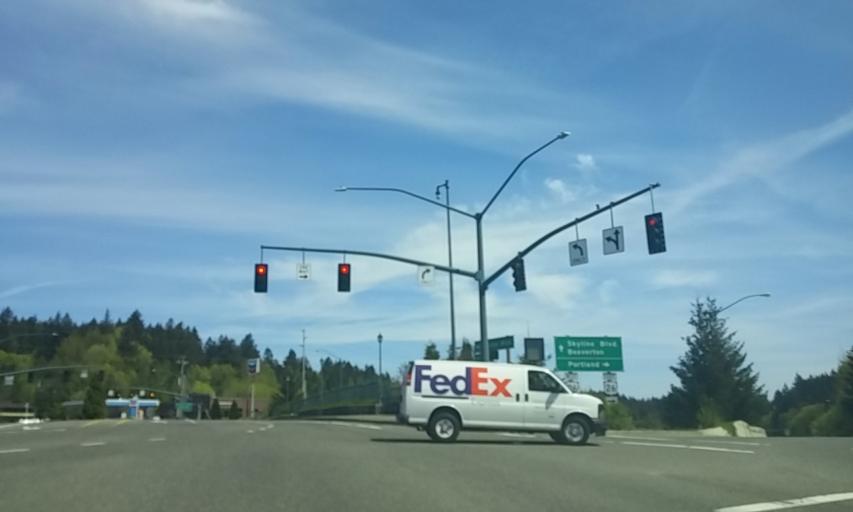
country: US
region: Oregon
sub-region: Washington County
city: West Slope
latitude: 45.5082
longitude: -122.7364
